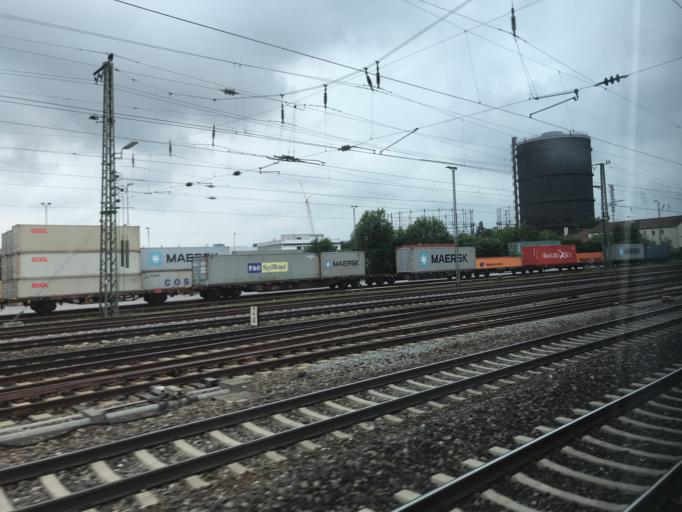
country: DE
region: Bavaria
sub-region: Swabia
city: Augsburg
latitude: 48.3839
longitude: 10.8714
